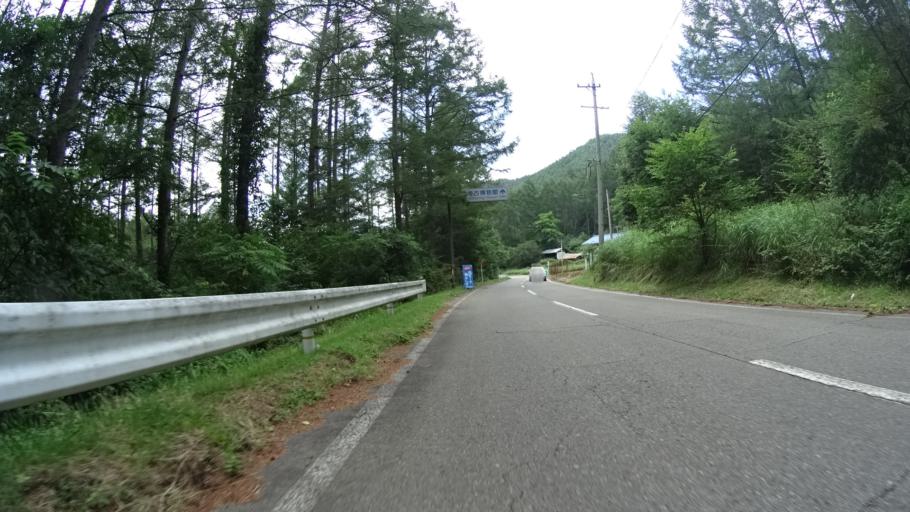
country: JP
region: Nagano
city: Saku
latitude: 36.0686
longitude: 138.6251
